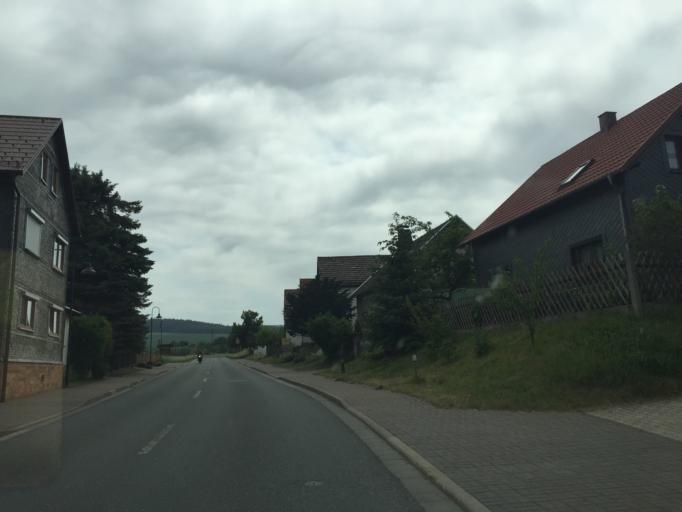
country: DE
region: Thuringia
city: Pennewitz
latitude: 50.6631
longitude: 11.0712
